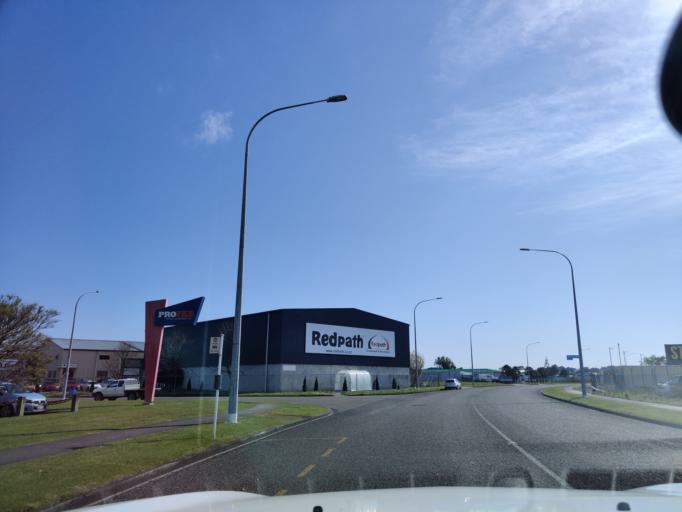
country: NZ
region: Manawatu-Wanganui
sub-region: Palmerston North City
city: Palmerston North
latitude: -40.3347
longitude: 175.6448
